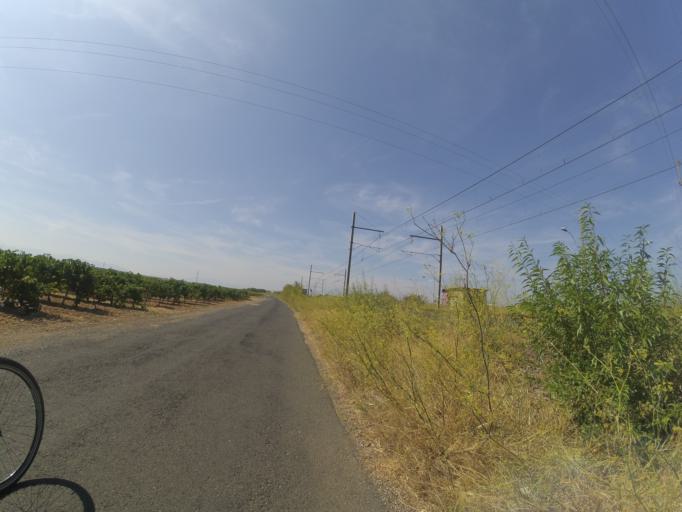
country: FR
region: Languedoc-Roussillon
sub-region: Departement des Pyrenees-Orientales
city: Salses-le-Chateau
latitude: 42.7988
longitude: 2.9010
